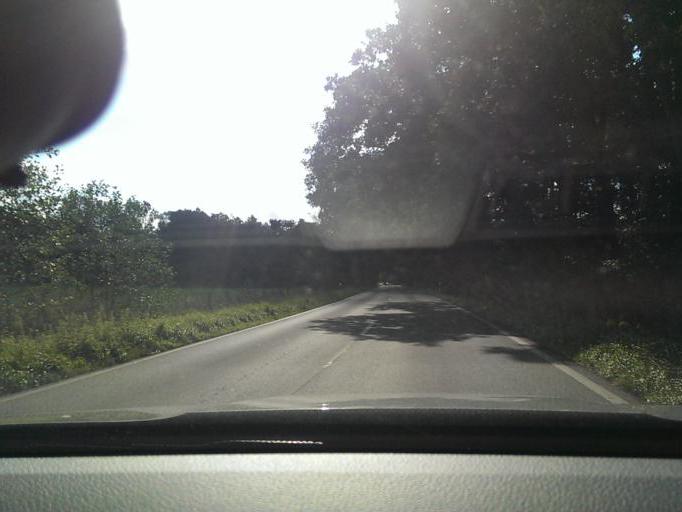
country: DE
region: Lower Saxony
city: Isernhagen Farster Bauerschaft
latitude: 52.5150
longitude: 9.8019
